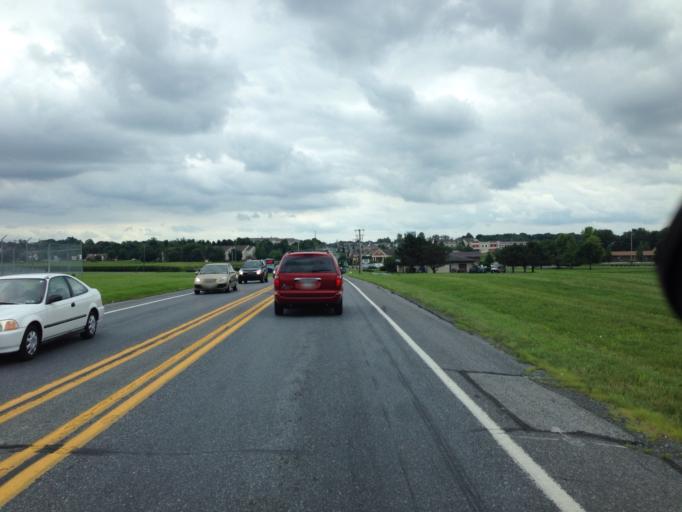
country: US
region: Pennsylvania
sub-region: Lancaster County
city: Lititz
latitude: 40.1186
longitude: -76.3058
